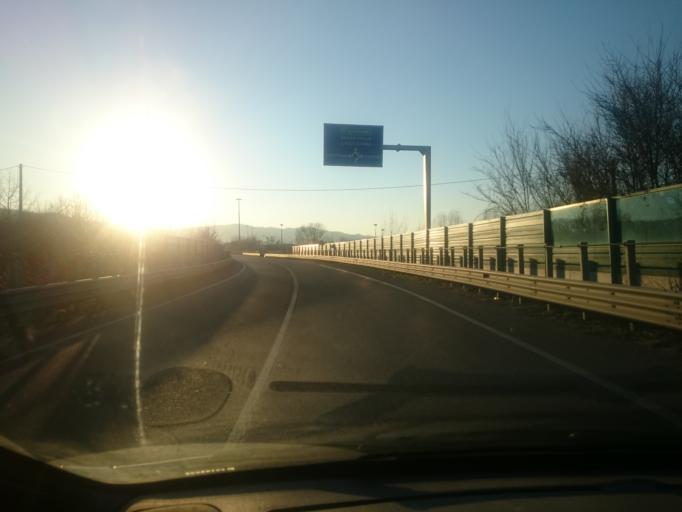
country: IT
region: Emilia-Romagna
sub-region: Provincia di Reggio Emilia
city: Scandiano
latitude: 44.5935
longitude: 10.7069
